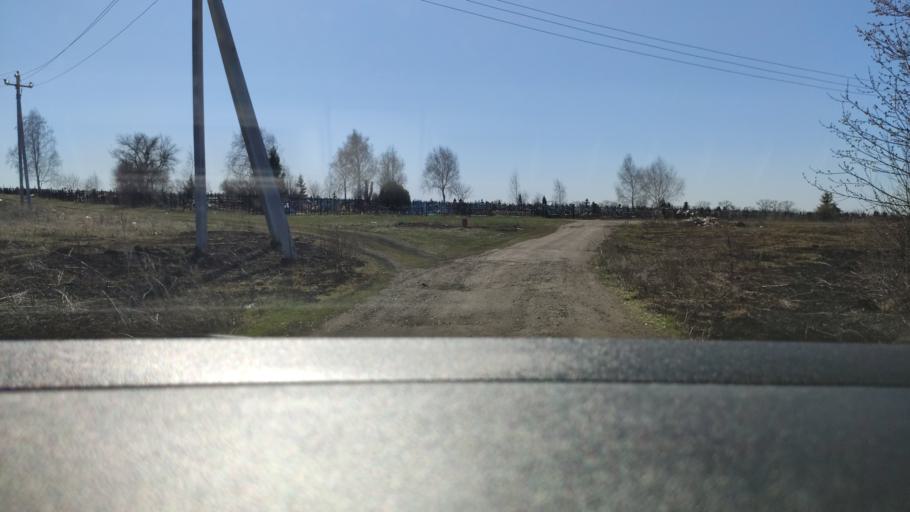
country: RU
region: Voronezj
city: Maslovka
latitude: 51.5003
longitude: 39.3050
